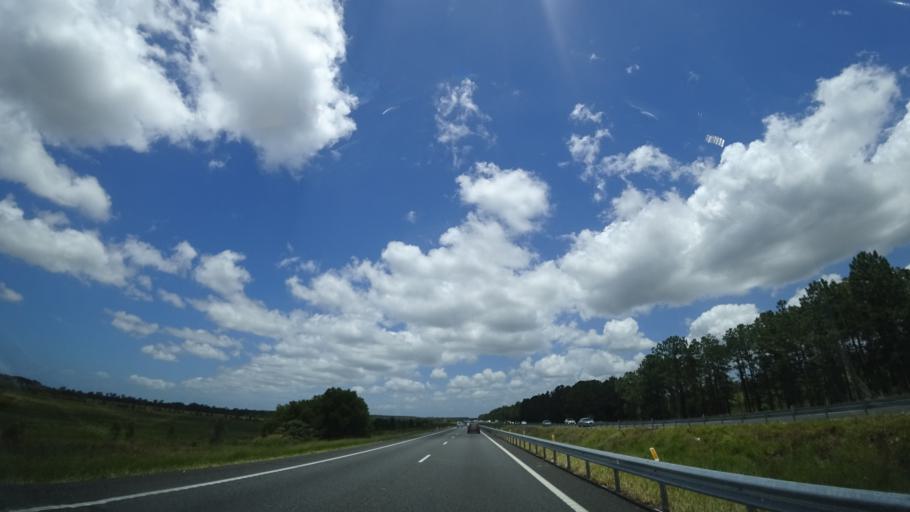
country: AU
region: Queensland
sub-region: Sunshine Coast
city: Little Mountain
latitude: -26.8269
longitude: 153.0347
